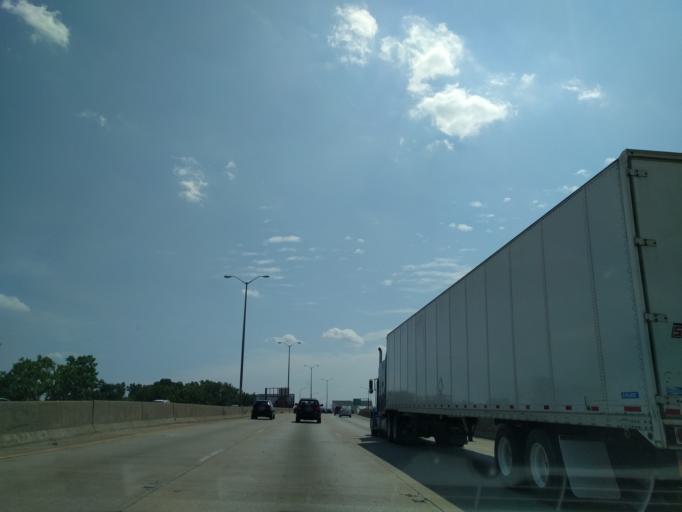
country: US
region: Illinois
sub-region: Cook County
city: Burnham
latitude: 41.6462
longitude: -87.5789
